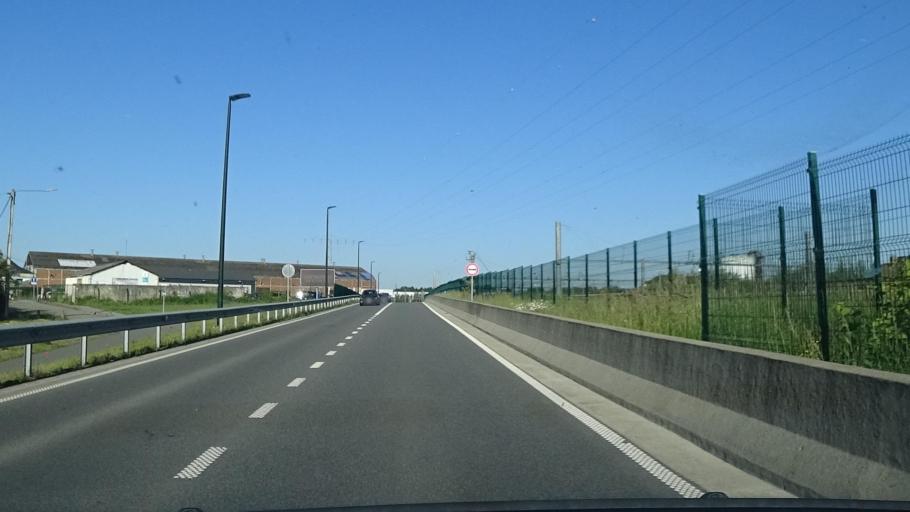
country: BE
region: Wallonia
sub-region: Province du Hainaut
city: La Louviere
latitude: 50.4851
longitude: 4.1880
